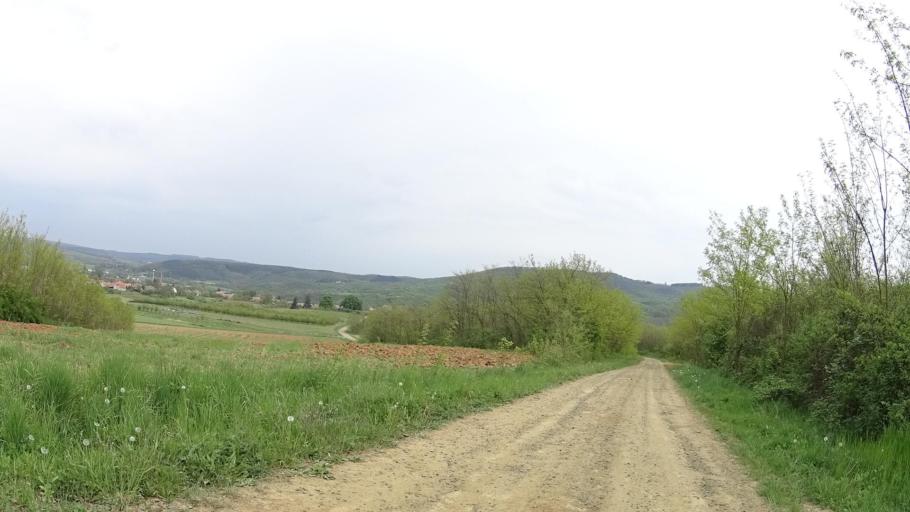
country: HU
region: Nograd
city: Romhany
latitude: 47.9116
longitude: 19.2542
